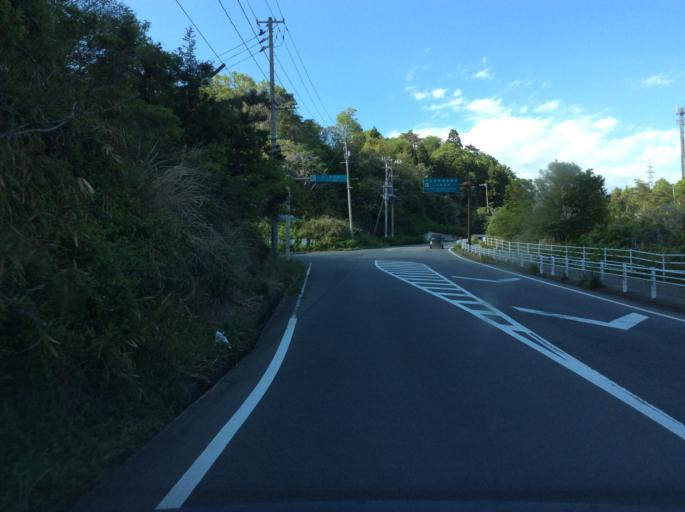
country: JP
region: Fukushima
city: Iwaki
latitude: 36.9632
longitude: 140.8491
